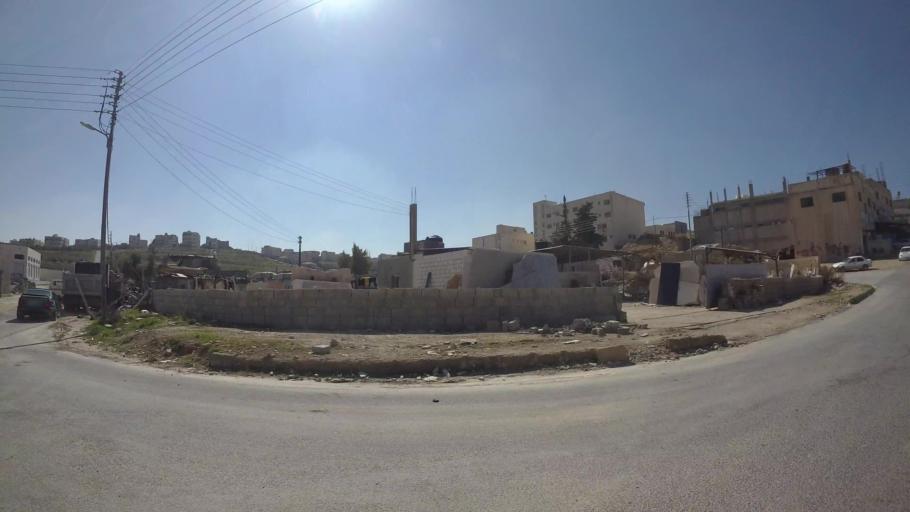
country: JO
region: Amman
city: Al Bunayyat ash Shamaliyah
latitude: 31.9118
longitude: 35.9092
